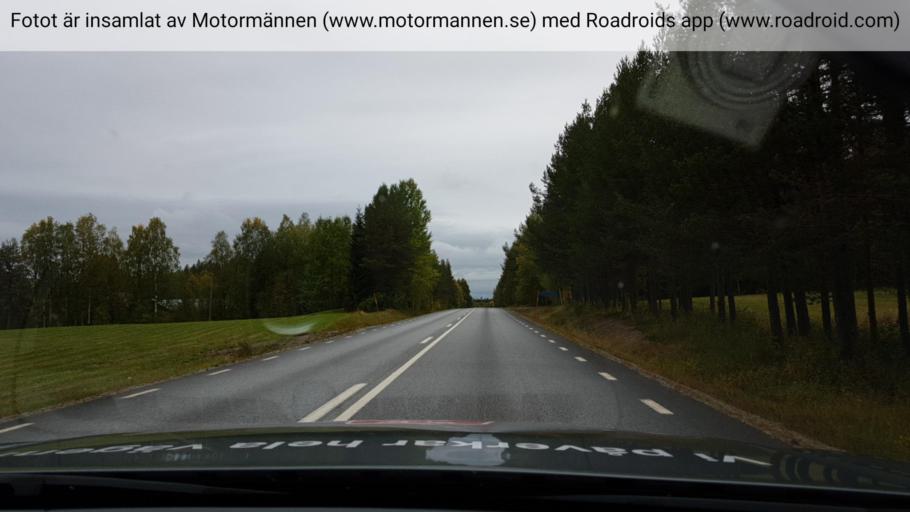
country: SE
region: Vaesterbotten
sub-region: Dorotea Kommun
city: Dorotea
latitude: 64.2450
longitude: 16.3240
